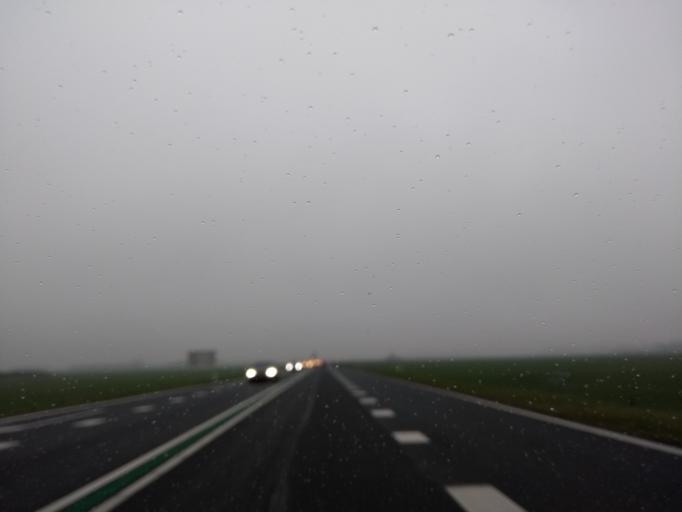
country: NL
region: Overijssel
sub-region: Gemeente Twenterand
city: Vriezenveen
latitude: 52.4183
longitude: 6.6322
